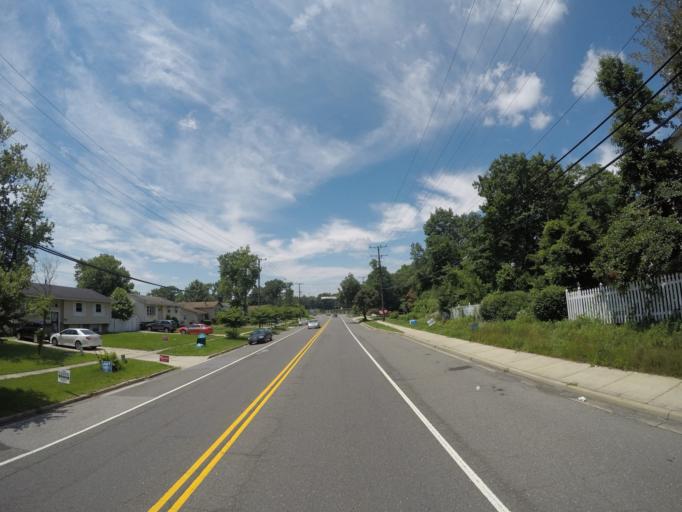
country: US
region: Maryland
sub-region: Prince George's County
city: New Carrollton
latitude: 38.9798
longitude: -76.8696
